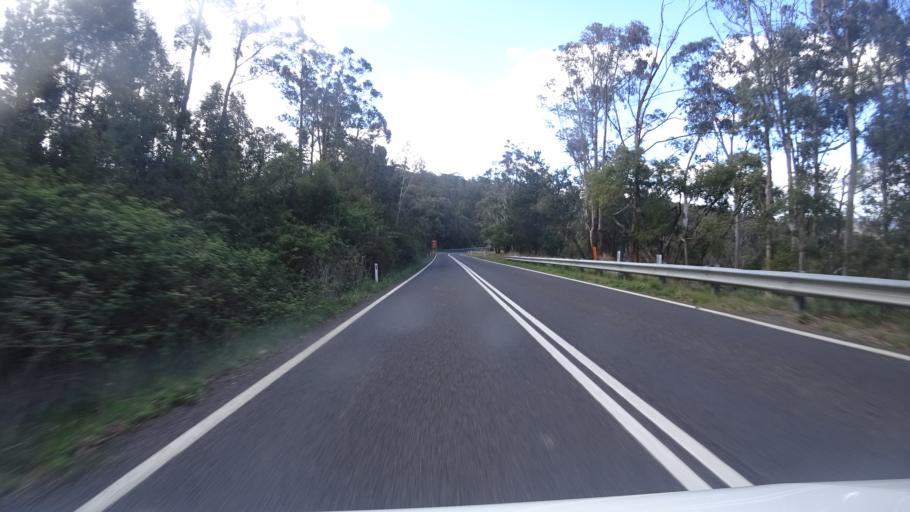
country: AU
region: New South Wales
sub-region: Lithgow
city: Bowenfels
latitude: -33.6603
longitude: 150.0519
